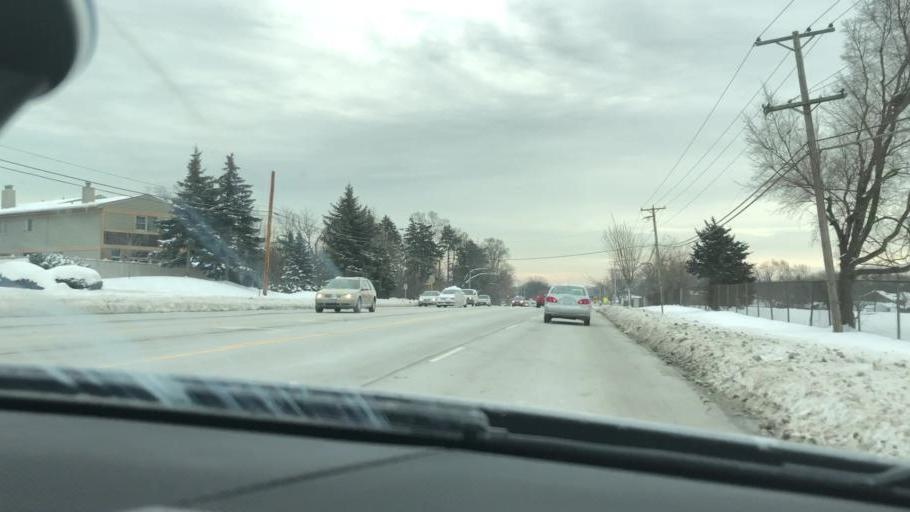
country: US
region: Illinois
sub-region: Cook County
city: Mount Prospect
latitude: 42.0760
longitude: -87.9304
